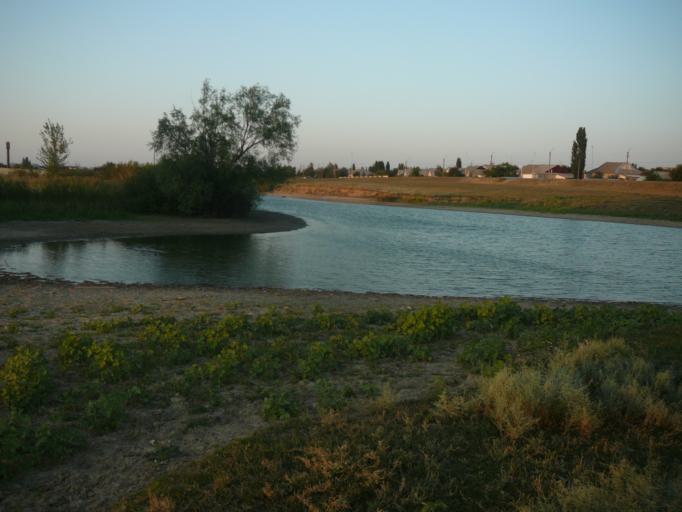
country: RU
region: Saratov
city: Stepnoye
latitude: 51.4273
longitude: 47.0036
